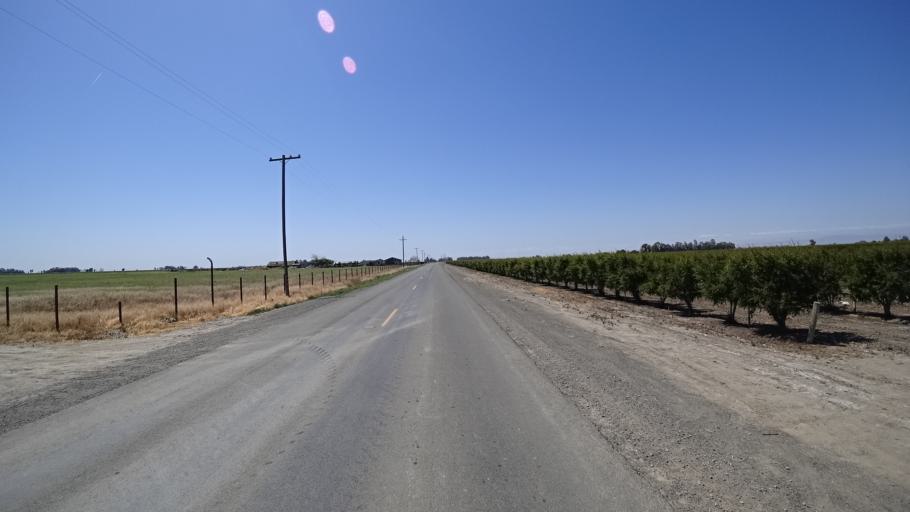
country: US
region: California
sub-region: Kings County
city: Stratford
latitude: 36.2189
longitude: -119.7982
